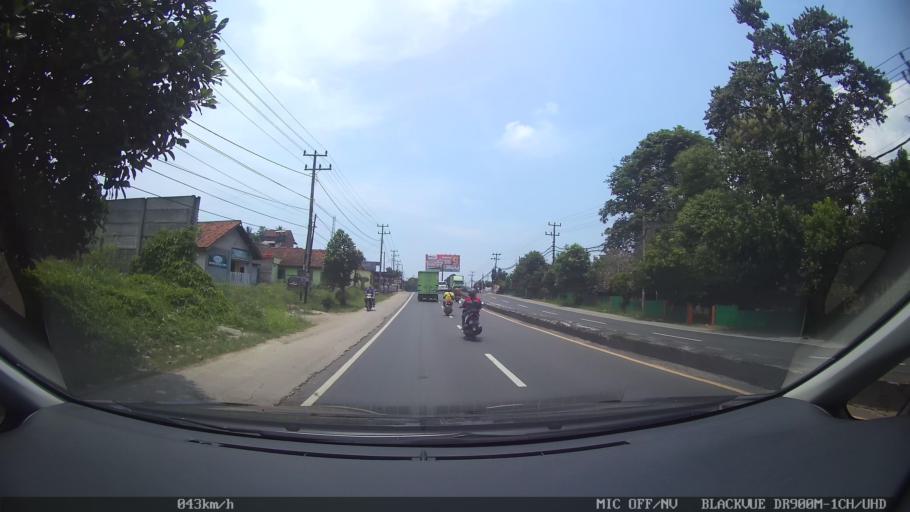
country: ID
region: Lampung
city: Natar
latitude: -5.3417
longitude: 105.2139
